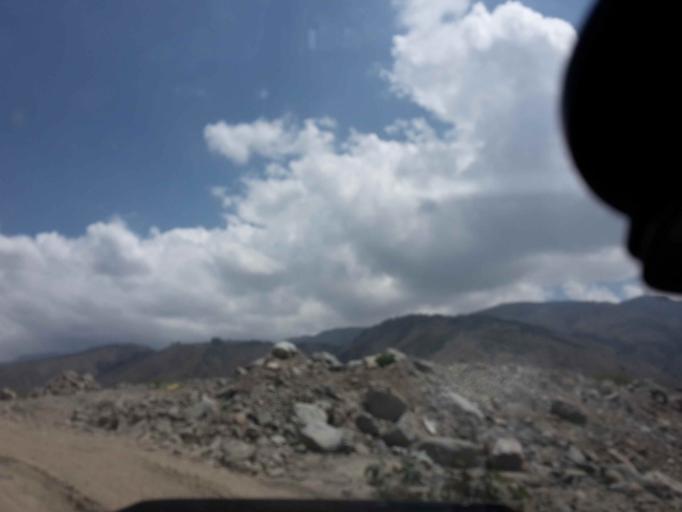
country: BO
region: Cochabamba
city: Cochabamba
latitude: -17.3312
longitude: -66.2117
